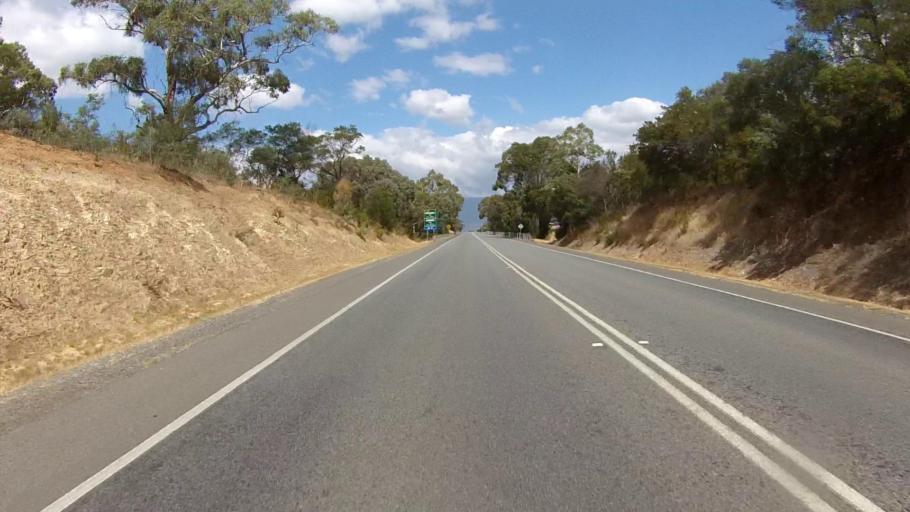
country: AU
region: Tasmania
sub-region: Brighton
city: Old Beach
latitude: -42.7676
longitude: 147.2699
